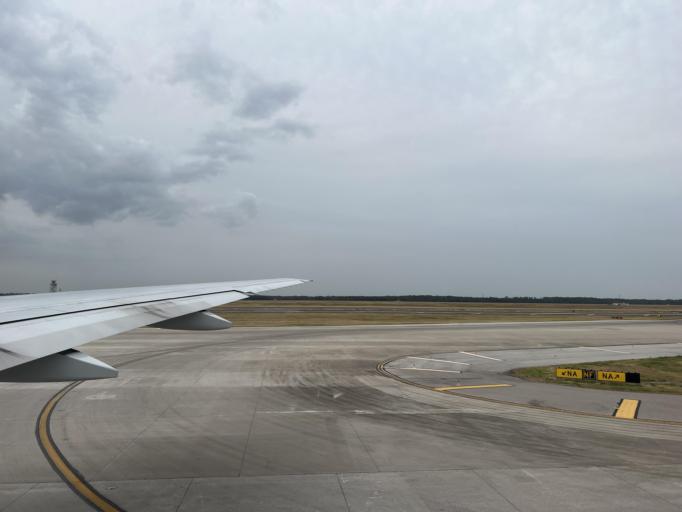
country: US
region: Texas
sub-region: Harris County
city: Aldine
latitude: 29.9908
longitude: -95.3501
